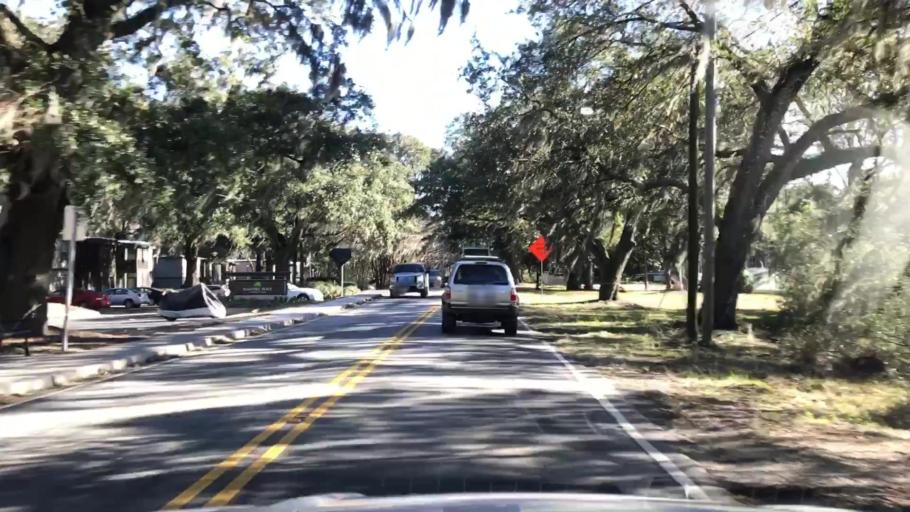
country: US
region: South Carolina
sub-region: Charleston County
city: North Charleston
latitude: 32.8185
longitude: -80.0340
